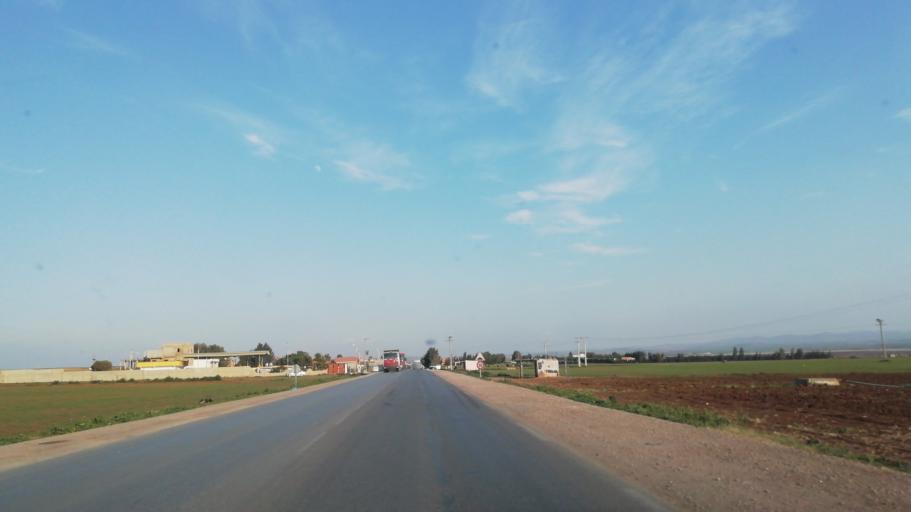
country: DZ
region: Relizane
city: Djidiouia
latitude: 35.8946
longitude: 0.6577
